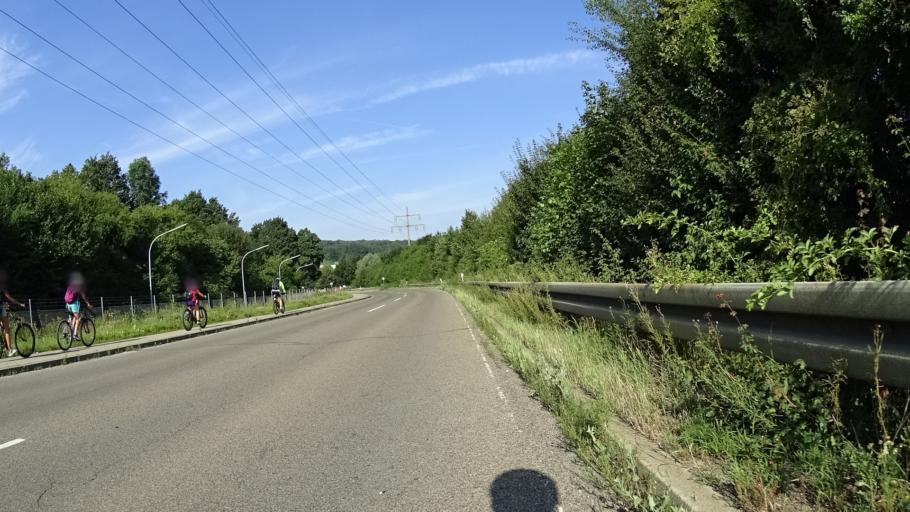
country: DE
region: Baden-Wuerttemberg
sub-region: Regierungsbezirk Stuttgart
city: Goeppingen
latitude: 48.6921
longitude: 9.6751
